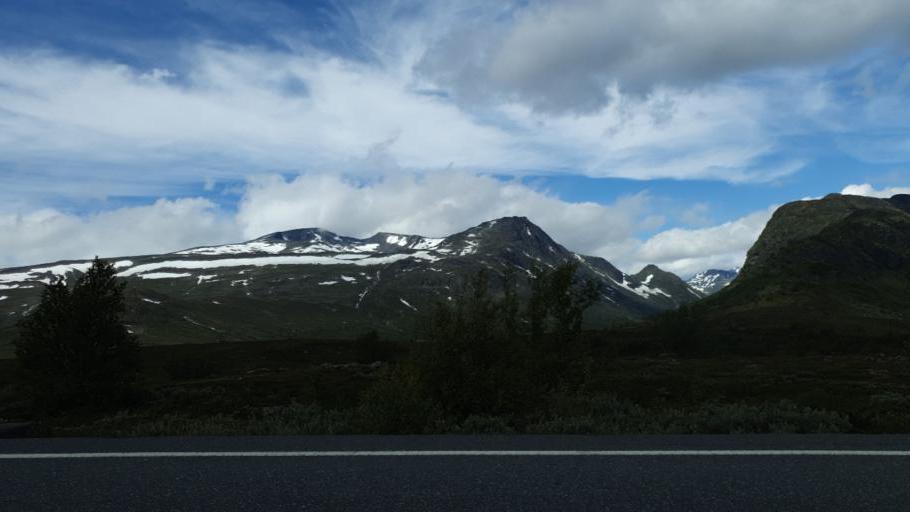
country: NO
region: Oppland
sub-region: Vang
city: Vang
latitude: 61.4625
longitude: 8.8064
